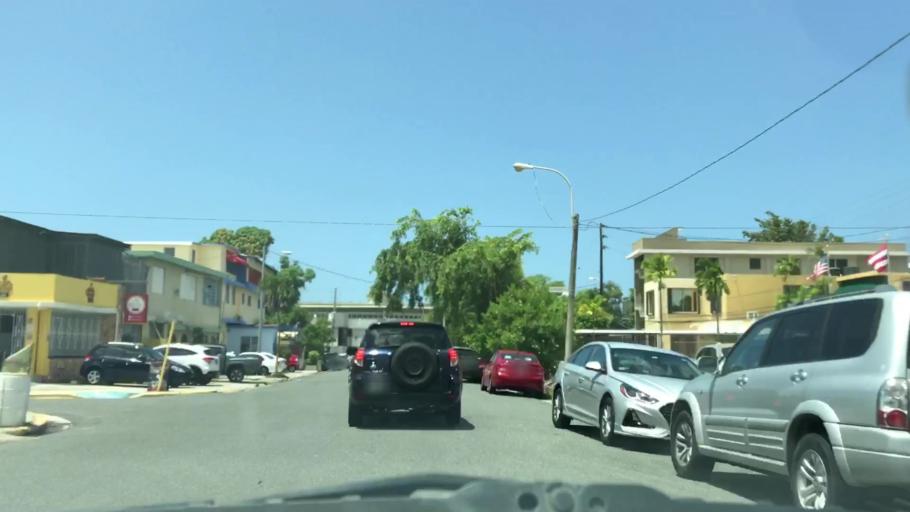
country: PR
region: Catano
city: Catano
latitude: 18.4188
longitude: -66.0625
